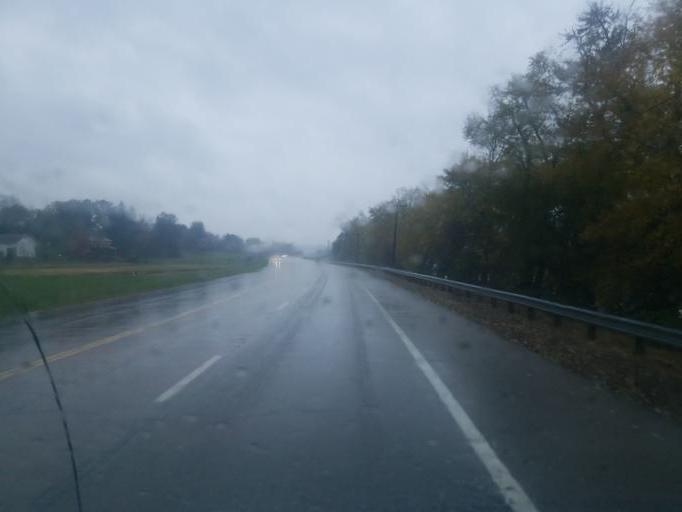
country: US
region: Ohio
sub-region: Muskingum County
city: South Zanesville
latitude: 39.8825
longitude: -81.9829
